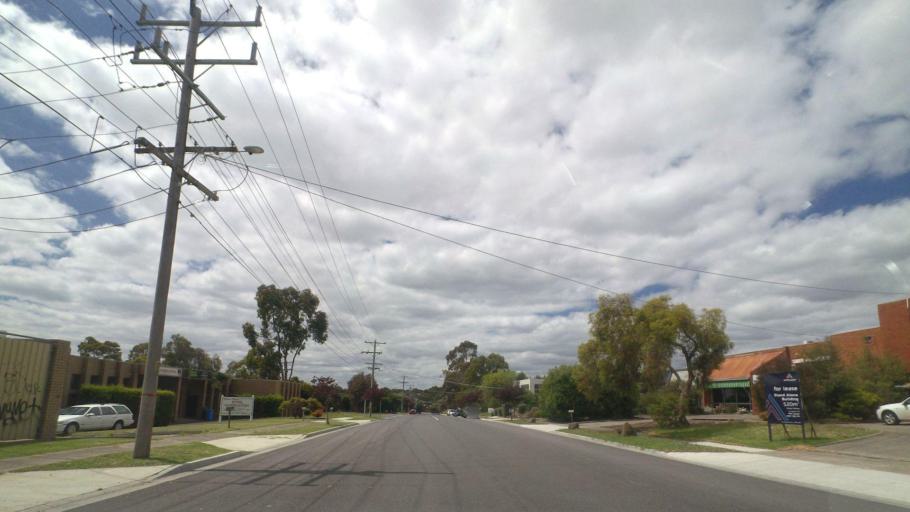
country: AU
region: Victoria
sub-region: Knox
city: Knoxfield
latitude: -37.8731
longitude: 145.2527
